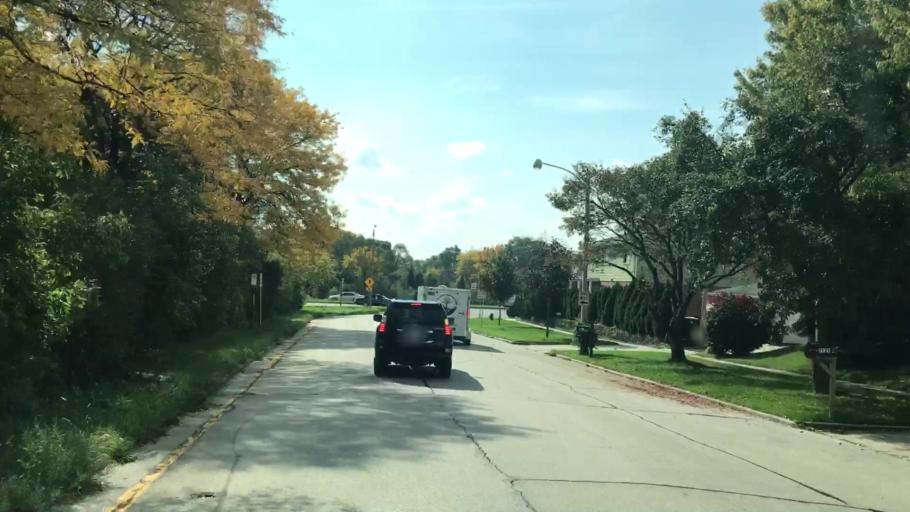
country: US
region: Wisconsin
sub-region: Waukesha County
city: Elm Grove
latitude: 43.0609
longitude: -88.0539
